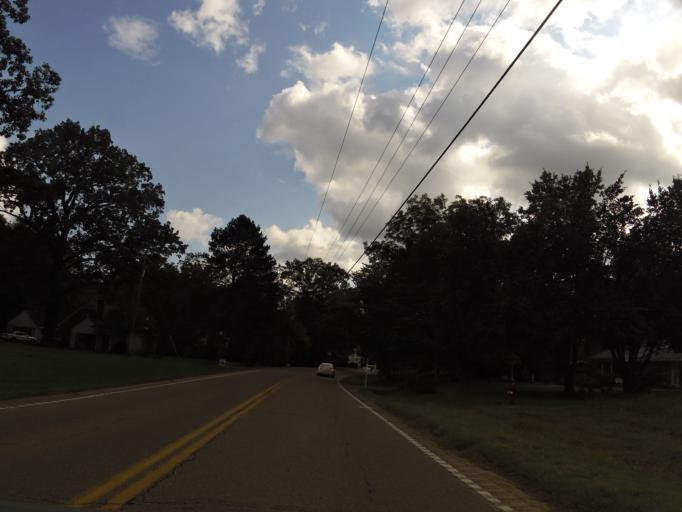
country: US
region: Mississippi
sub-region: Alcorn County
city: Farmington
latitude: 35.0089
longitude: -88.4595
